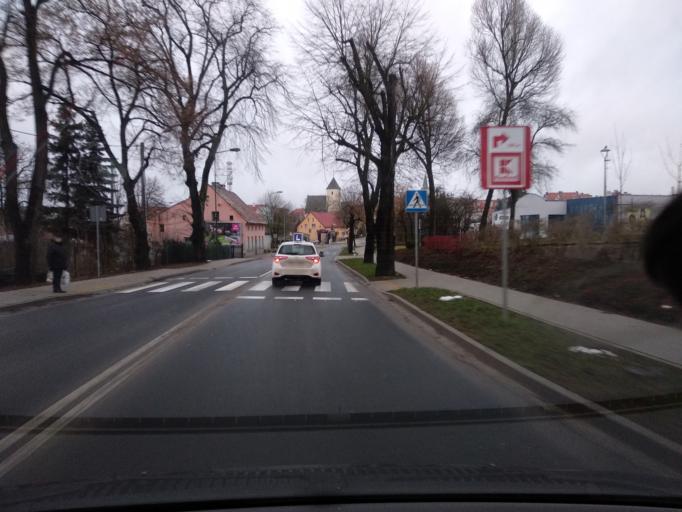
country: PL
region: Lower Silesian Voivodeship
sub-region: Powiat polkowicki
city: Polkowice
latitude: 51.5000
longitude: 16.0684
